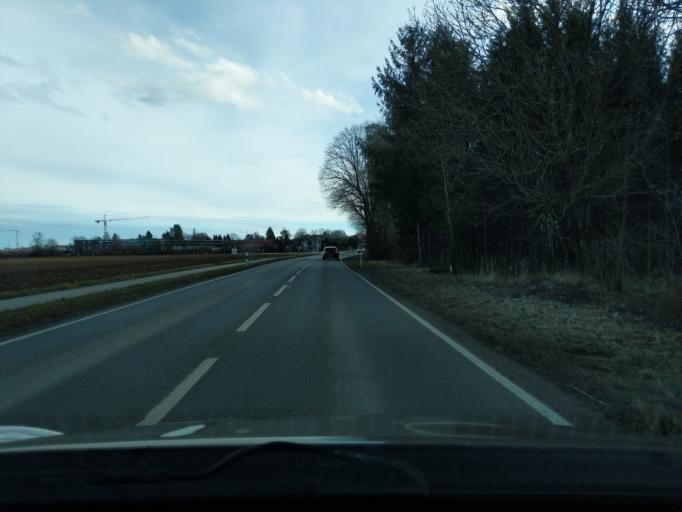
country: DE
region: Bavaria
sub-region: Upper Bavaria
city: Vaterstetten
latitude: 48.1178
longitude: 11.7685
